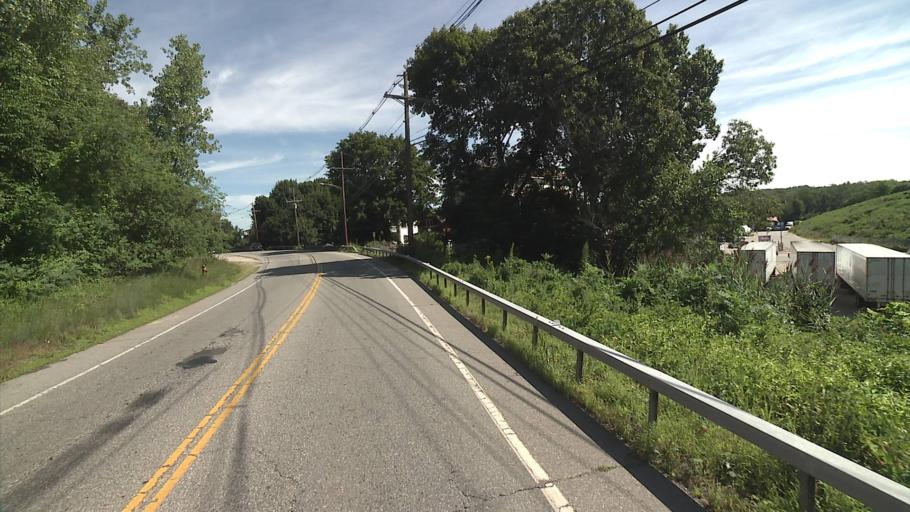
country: US
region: Connecticut
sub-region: New London County
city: Norwich
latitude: 41.5587
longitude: -72.0485
